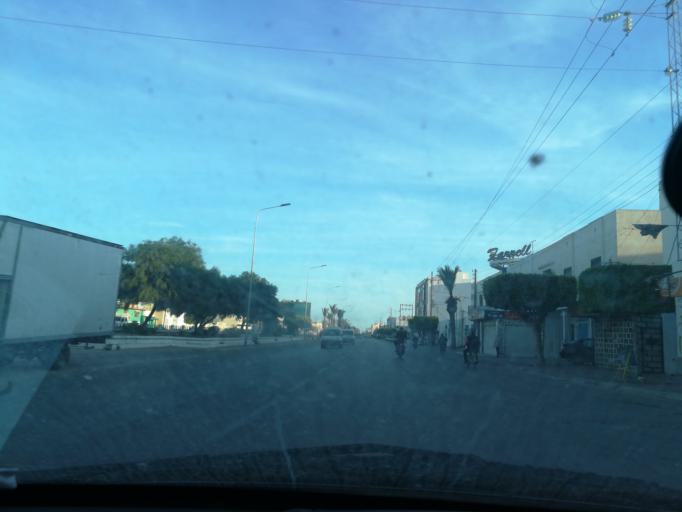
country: TN
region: Safaqis
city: Al Qarmadah
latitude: 34.8188
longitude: 10.7623
